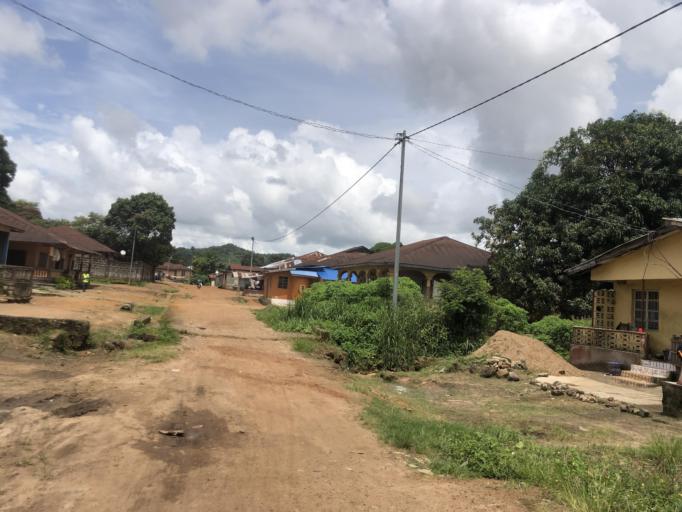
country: SL
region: Northern Province
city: Makeni
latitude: 8.8806
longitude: -12.0505
